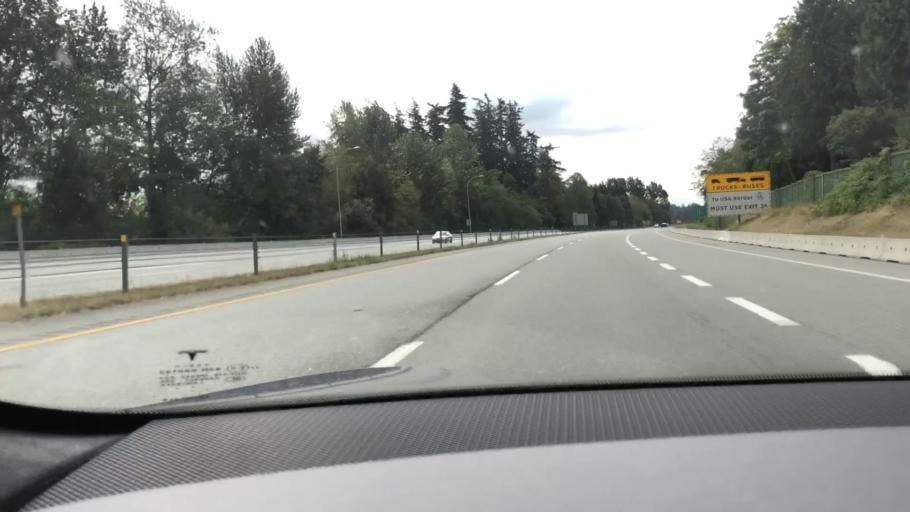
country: CA
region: British Columbia
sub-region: Greater Vancouver Regional District
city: White Rock
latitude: 49.0284
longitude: -122.7665
